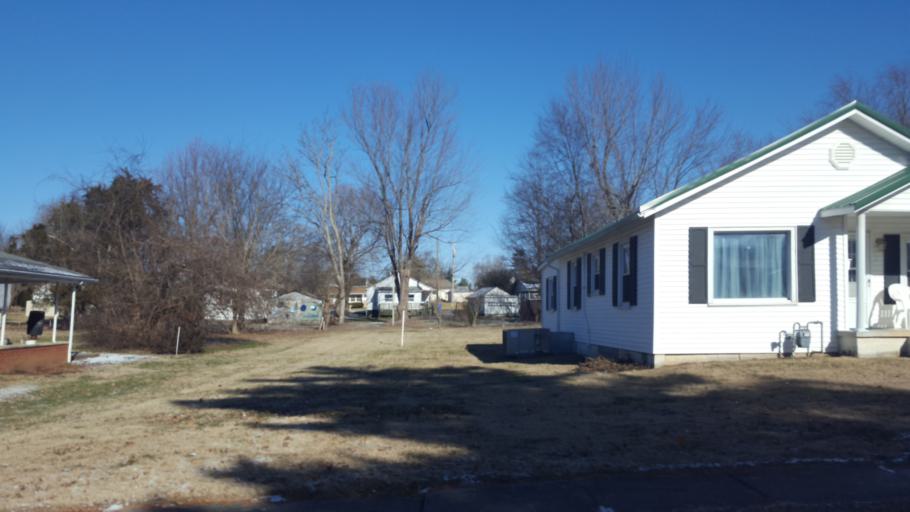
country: US
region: Kentucky
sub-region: Crittenden County
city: Marion
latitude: 37.3316
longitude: -88.0860
